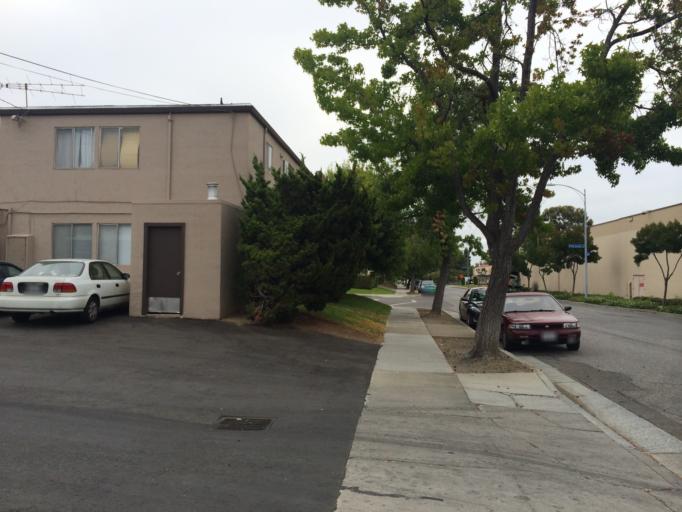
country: US
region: California
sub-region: Santa Clara County
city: Cupertino
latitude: 37.3252
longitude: -122.0365
